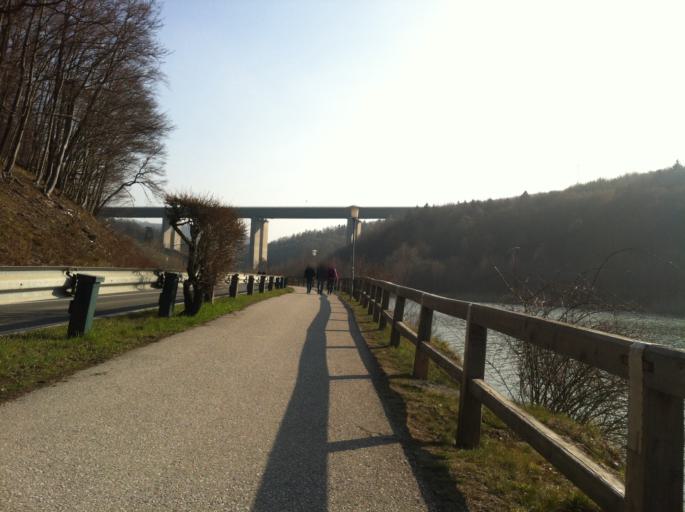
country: AT
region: Lower Austria
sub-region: Politischer Bezirk Wien-Umgebung
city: Wolfsgraben
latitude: 48.1797
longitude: 16.1226
